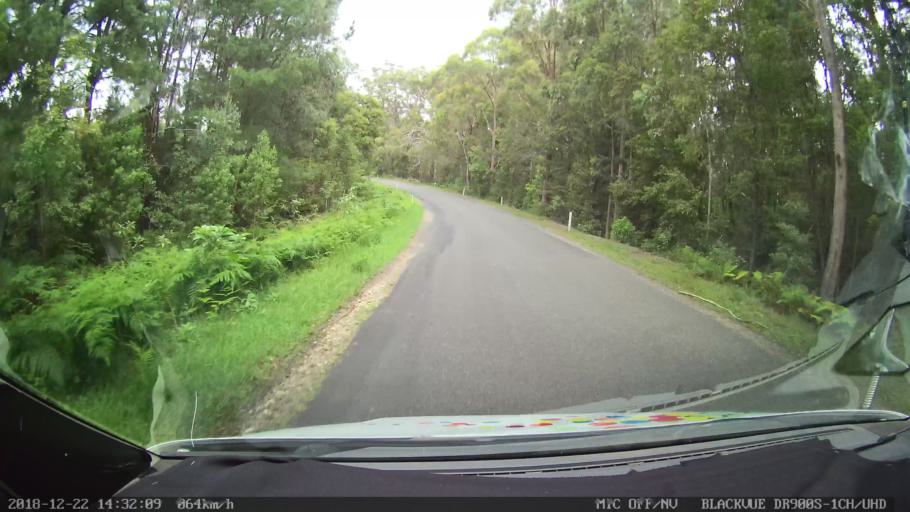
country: AU
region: New South Wales
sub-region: Bellingen
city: Dorrigo
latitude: -30.1011
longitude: 152.6276
